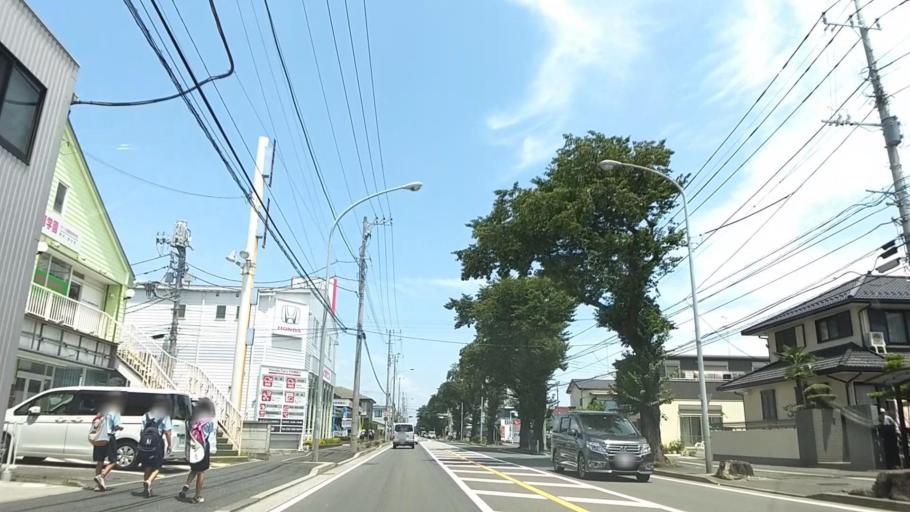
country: JP
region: Kanagawa
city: Minami-rinkan
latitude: 35.4769
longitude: 139.4805
